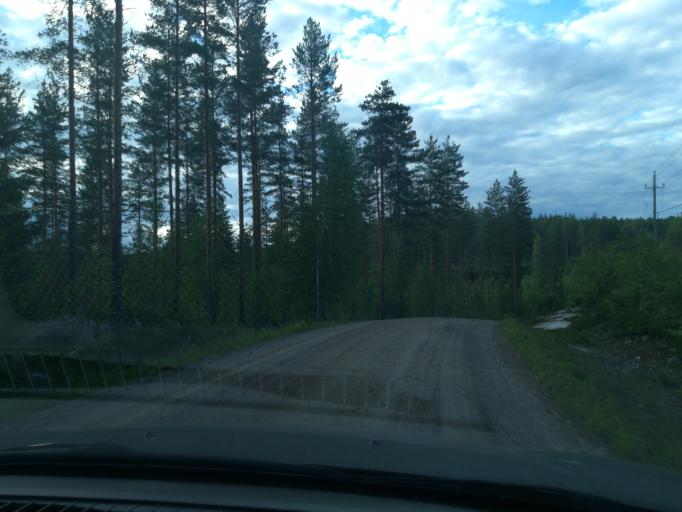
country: FI
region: Southern Savonia
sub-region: Mikkeli
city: Puumala
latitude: 61.5981
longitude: 28.1480
